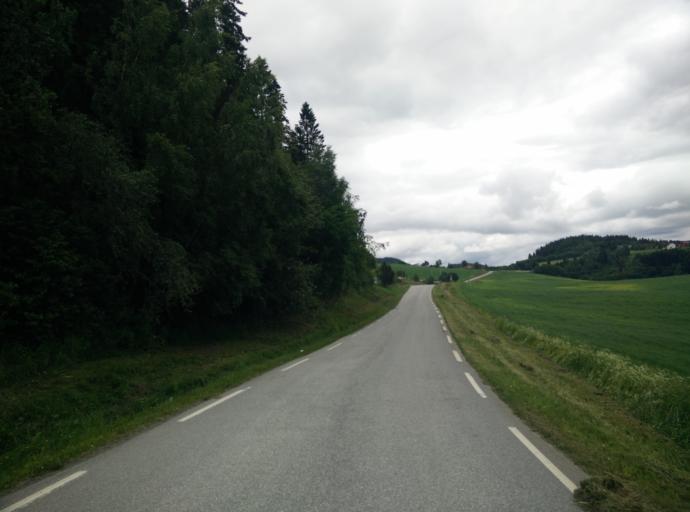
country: NO
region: Sor-Trondelag
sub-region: Skaun
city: Borsa
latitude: 63.3203
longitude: 10.0778
